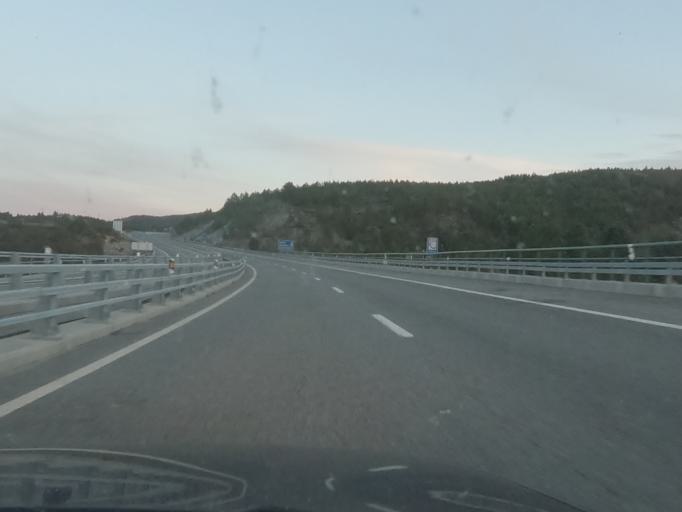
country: PT
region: Vila Real
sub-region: Vila Pouca de Aguiar
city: Vila Pouca de Aguiar
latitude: 41.5773
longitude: -7.6427
